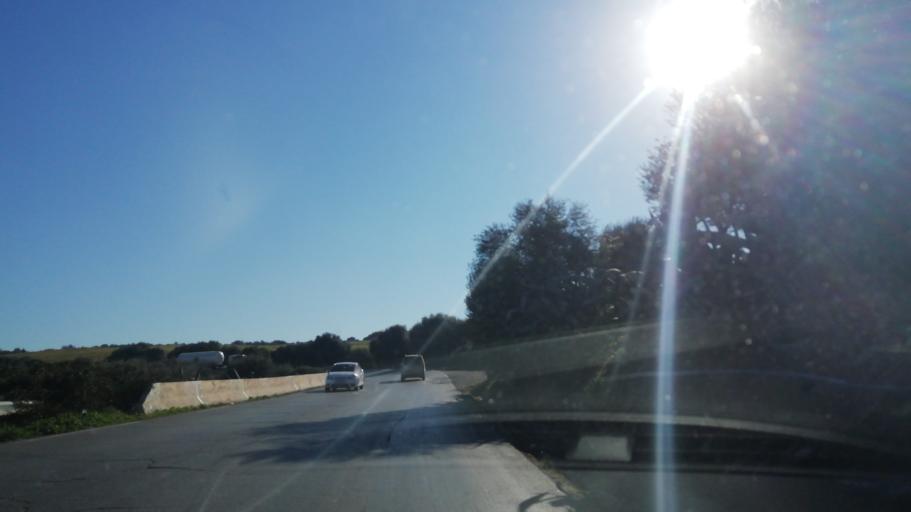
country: DZ
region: Relizane
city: Smala
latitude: 35.7039
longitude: 0.7697
